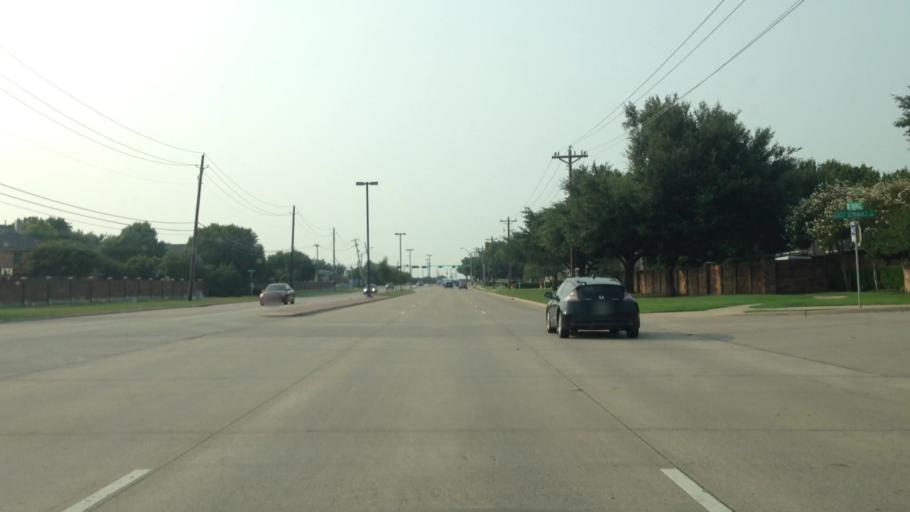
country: US
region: Texas
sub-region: Dallas County
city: Carrollton
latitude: 33.0135
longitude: -96.9123
